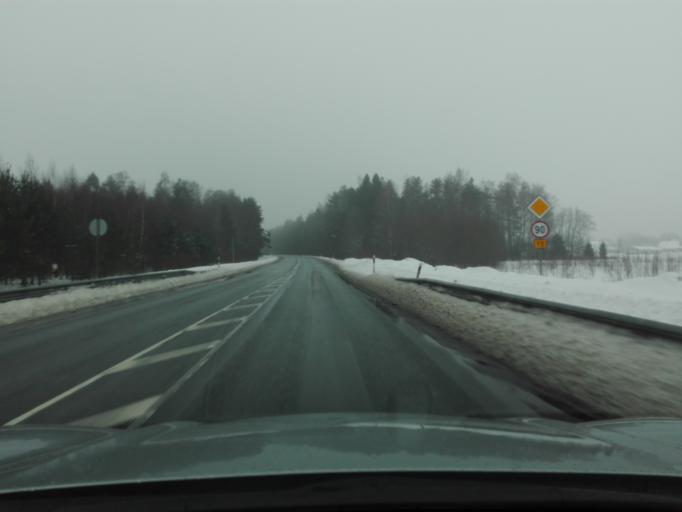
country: EE
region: Raplamaa
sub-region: Kohila vald
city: Kohila
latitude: 59.1686
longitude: 24.7716
